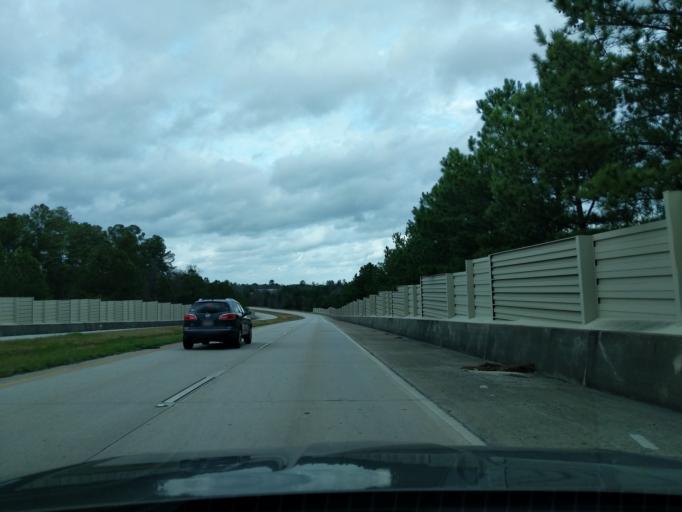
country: US
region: Georgia
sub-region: Columbia County
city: Martinez
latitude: 33.4622
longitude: -82.1188
